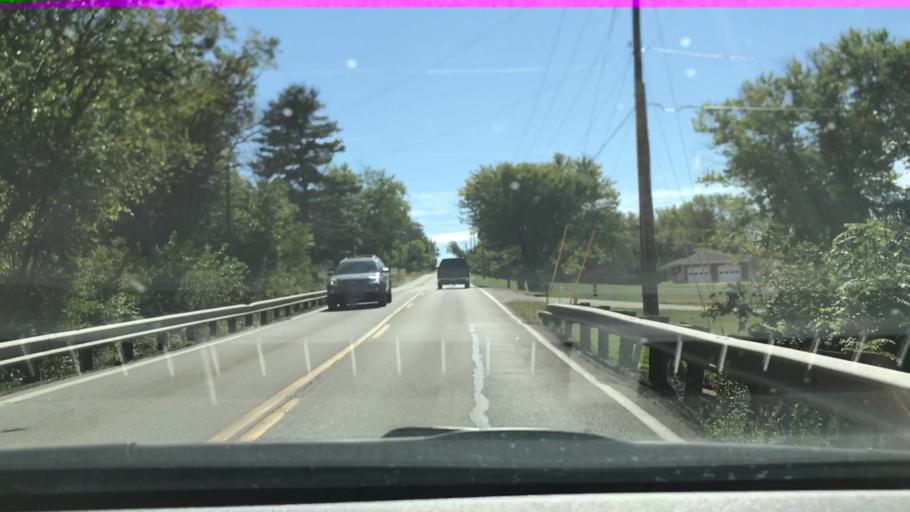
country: US
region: Ohio
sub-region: Butler County
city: Hamilton
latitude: 39.4530
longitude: -84.6227
